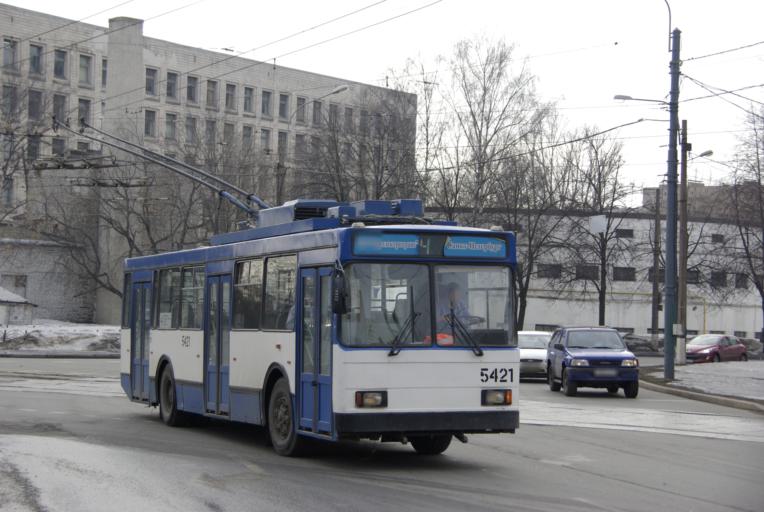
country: RU
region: St.-Petersburg
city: Kushelevka
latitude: 59.9975
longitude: 30.3647
